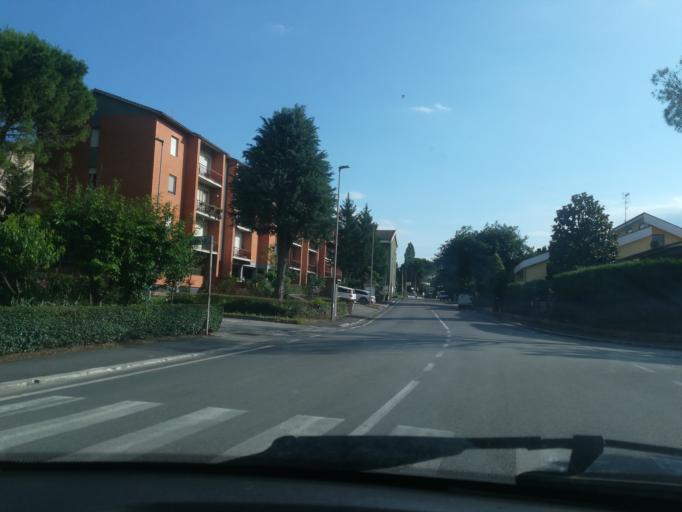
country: IT
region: The Marches
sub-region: Provincia di Macerata
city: Villa Potenza
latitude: 43.3192
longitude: 13.4226
